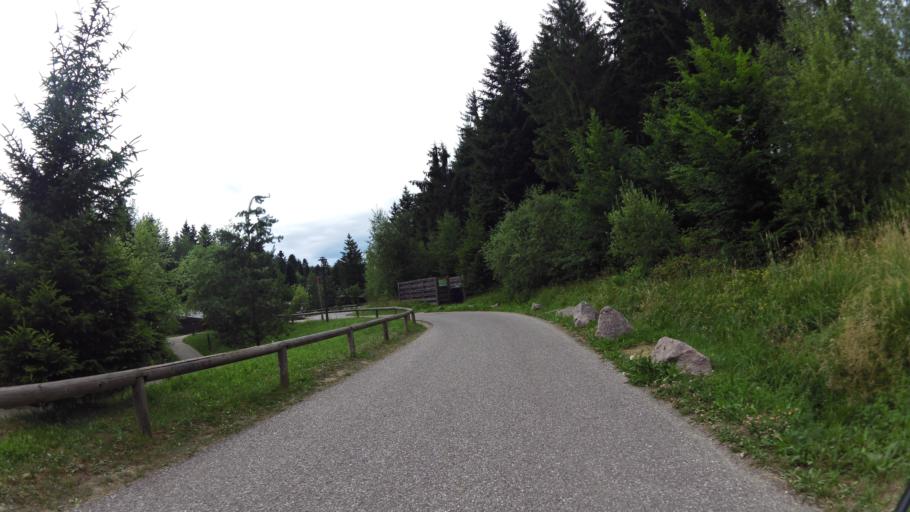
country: FR
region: Lorraine
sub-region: Departement de la Moselle
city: Lorquin
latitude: 48.6231
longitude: 6.9930
